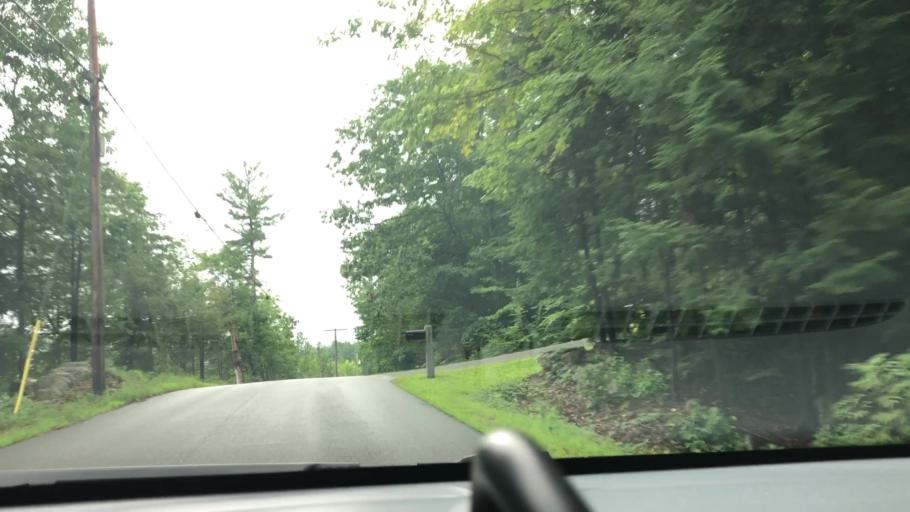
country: US
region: New Hampshire
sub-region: Hillsborough County
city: Pinardville
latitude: 42.9856
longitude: -71.5342
